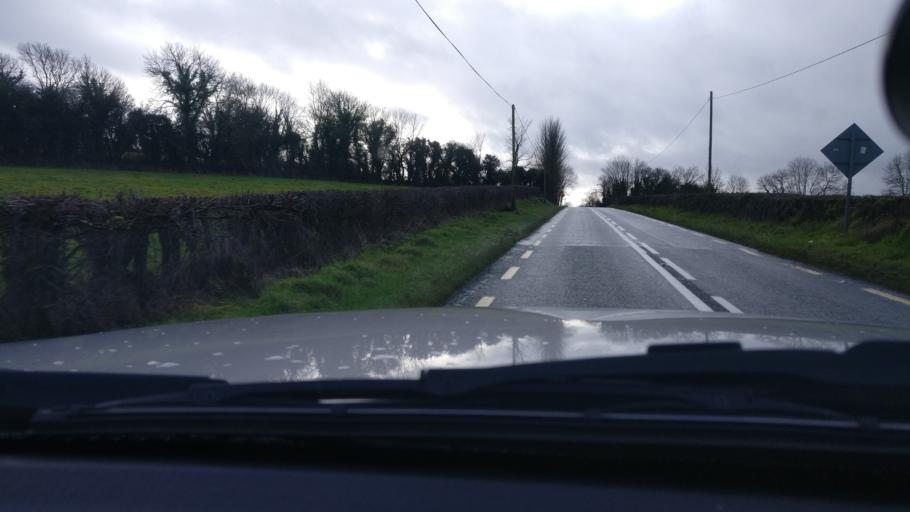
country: IE
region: Leinster
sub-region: An Iarmhi
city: Moate
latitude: 53.6191
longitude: -7.7016
